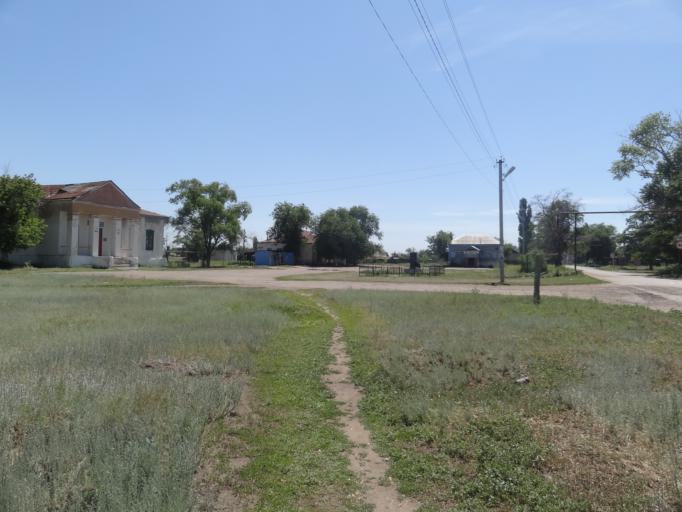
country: RU
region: Saratov
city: Krasnoarmeysk
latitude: 51.1177
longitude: 45.9482
